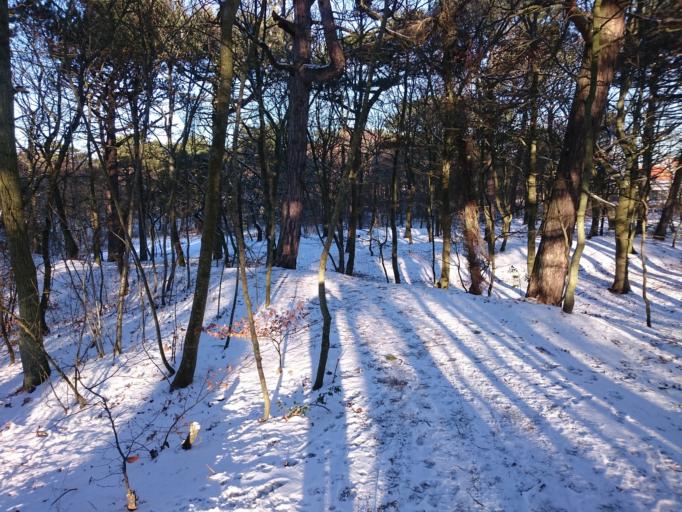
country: DK
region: North Denmark
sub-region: Frederikshavn Kommune
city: Skagen
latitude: 57.7184
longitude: 10.5742
